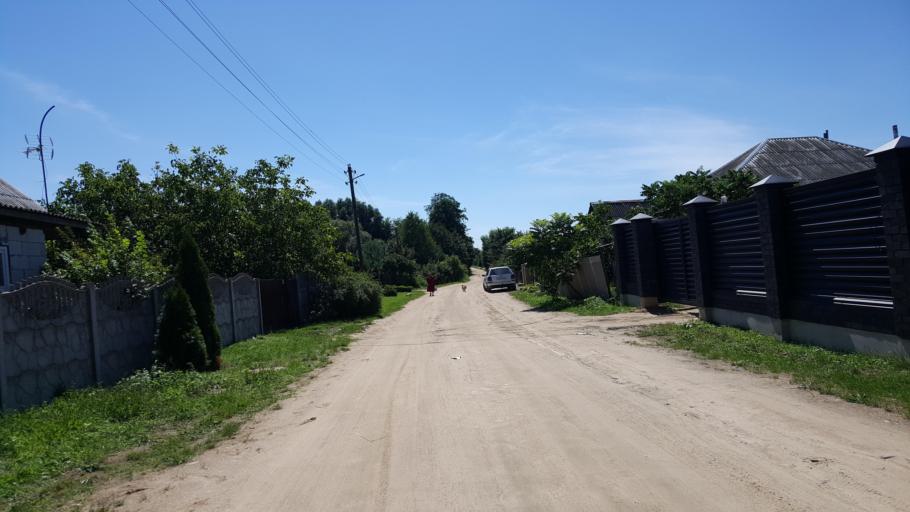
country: BY
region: Brest
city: Charnawchytsy
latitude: 52.2293
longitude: 23.7798
